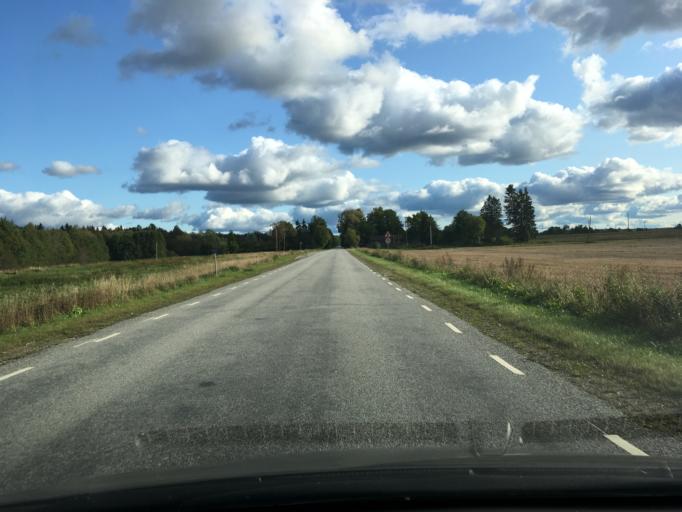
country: EE
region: Harju
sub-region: Raasiku vald
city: Raasiku
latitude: 59.3109
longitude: 25.1641
